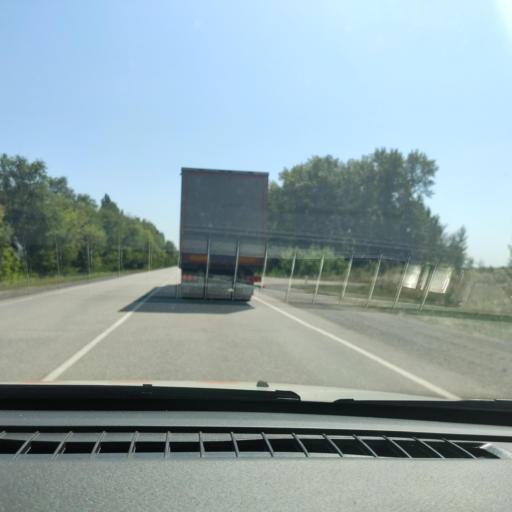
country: RU
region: Voronezj
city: Ostrogozhsk
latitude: 50.9665
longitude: 39.0111
